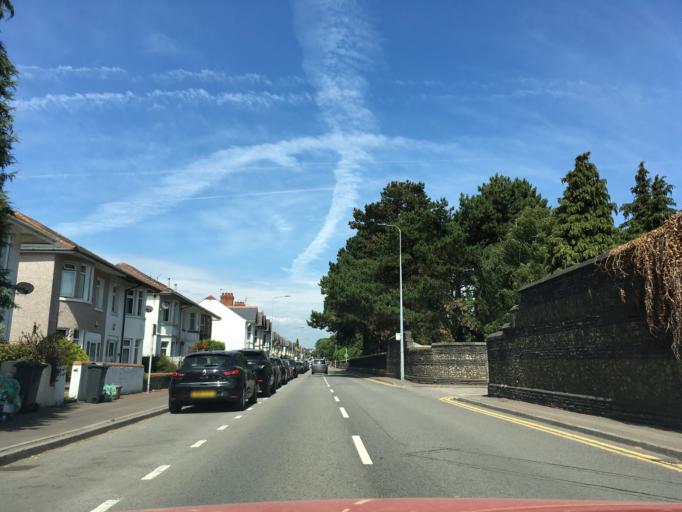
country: GB
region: Wales
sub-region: Cardiff
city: Cardiff
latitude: 51.5059
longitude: -3.1832
